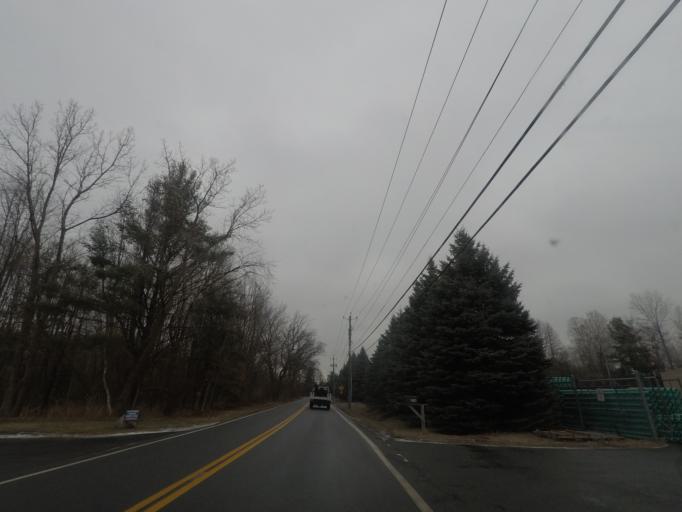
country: US
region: New York
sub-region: Saratoga County
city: Country Knolls
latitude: 42.9059
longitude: -73.7768
